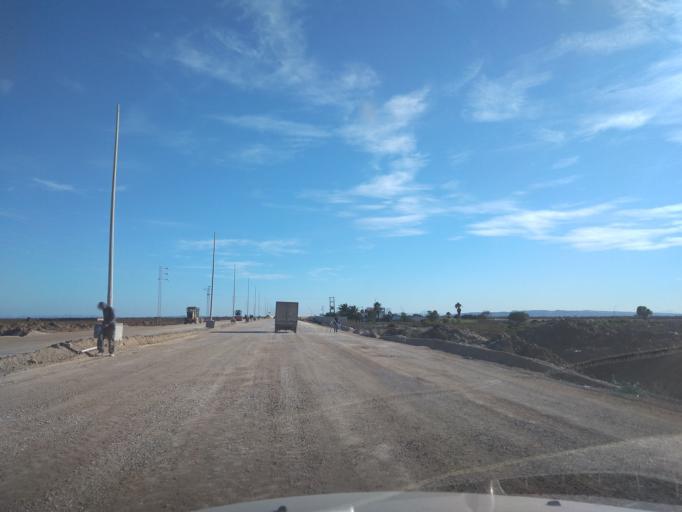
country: TN
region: Ariana
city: Qal'at al Andalus
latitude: 37.0441
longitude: 10.1277
